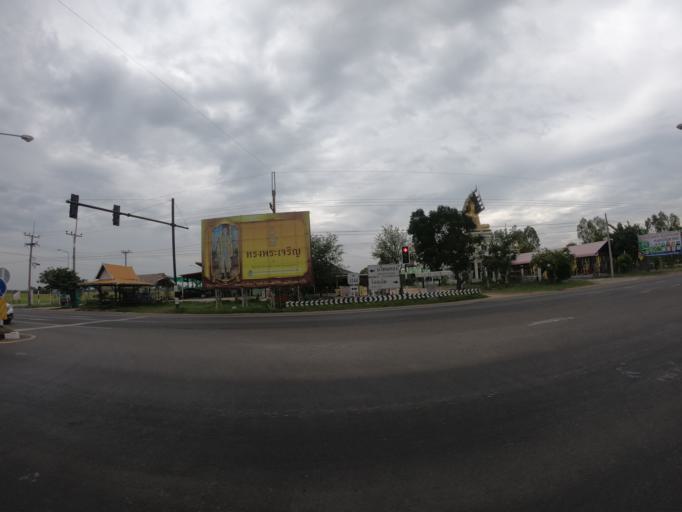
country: TH
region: Roi Et
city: Thawat Buri
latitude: 16.0922
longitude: 103.7792
